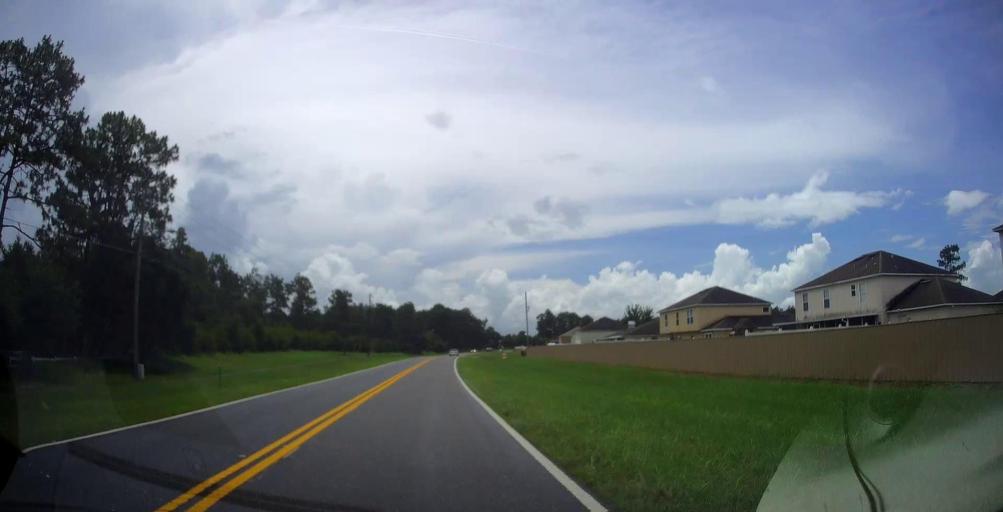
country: US
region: Florida
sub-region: Marion County
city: Silver Springs Shores
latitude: 29.1258
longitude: -82.0189
